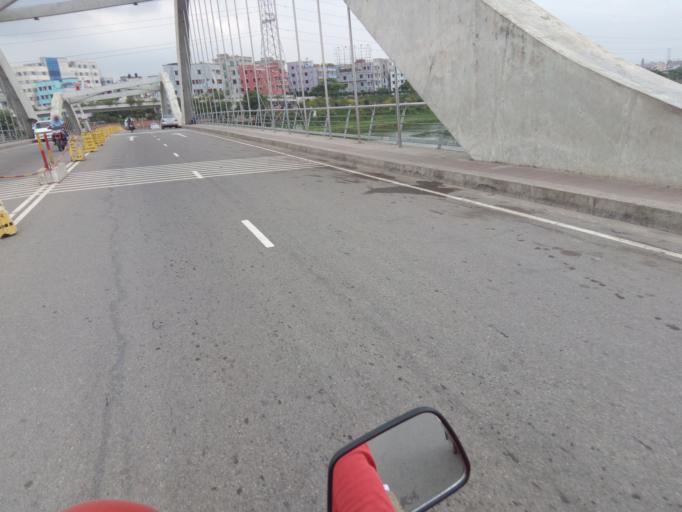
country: BD
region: Dhaka
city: Paltan
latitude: 23.7681
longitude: 90.4127
